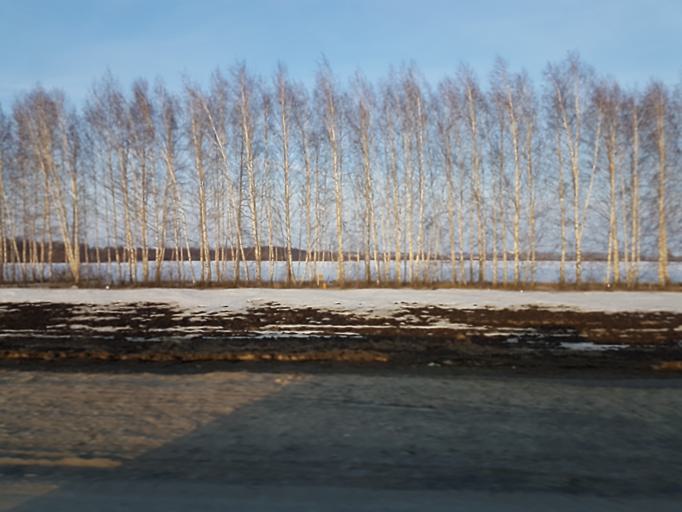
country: RU
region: Tambov
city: Zavoronezhskoye
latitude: 52.8618
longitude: 40.7667
